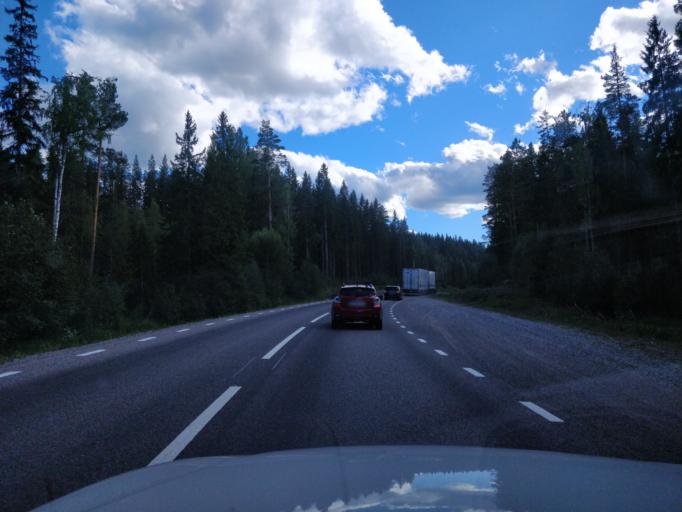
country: SE
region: Dalarna
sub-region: Ludvika Kommun
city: Abborrberget
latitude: 60.1992
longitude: 14.8387
